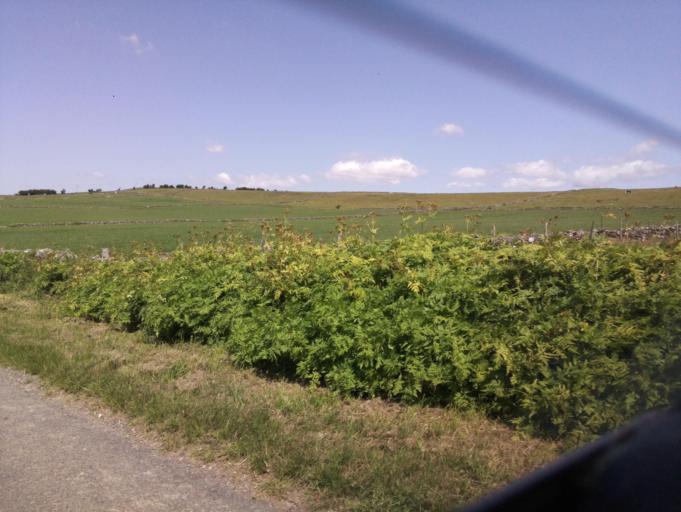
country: GB
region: England
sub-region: Derbyshire
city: Buxton
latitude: 53.2793
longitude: -1.8468
